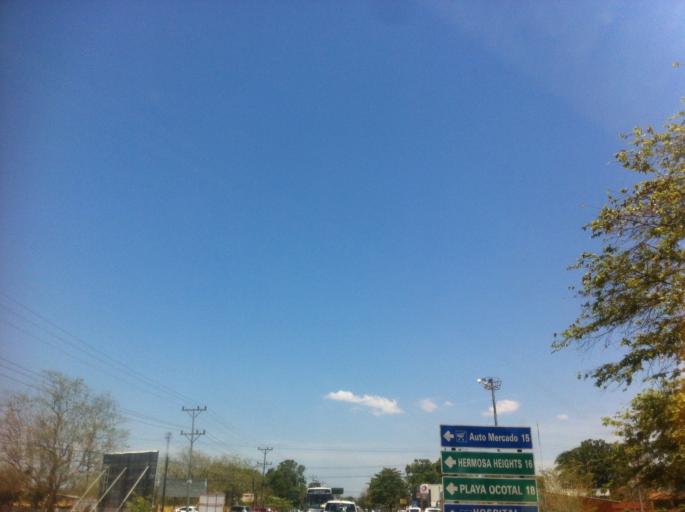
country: CR
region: Guanacaste
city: Sardinal
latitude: 10.5390
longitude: -85.5864
